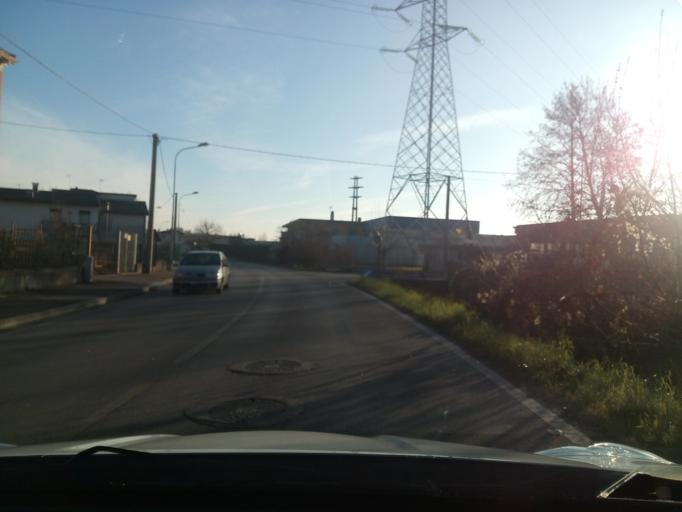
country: IT
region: Veneto
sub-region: Provincia di Vicenza
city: Dueville
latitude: 45.6290
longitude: 11.5508
